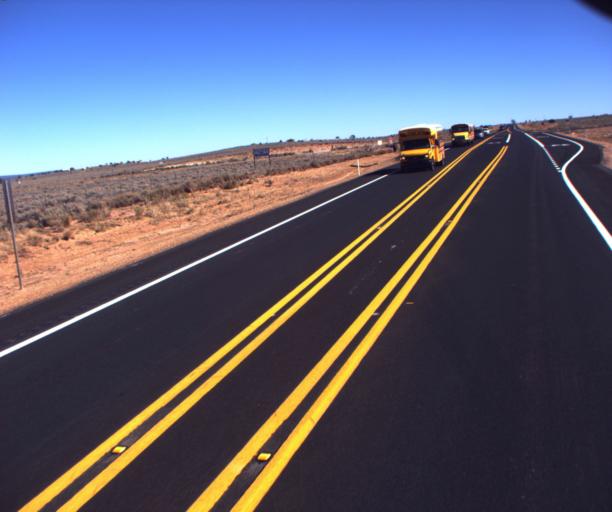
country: US
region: Arizona
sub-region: Apache County
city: Ganado
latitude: 35.7165
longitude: -109.4538
